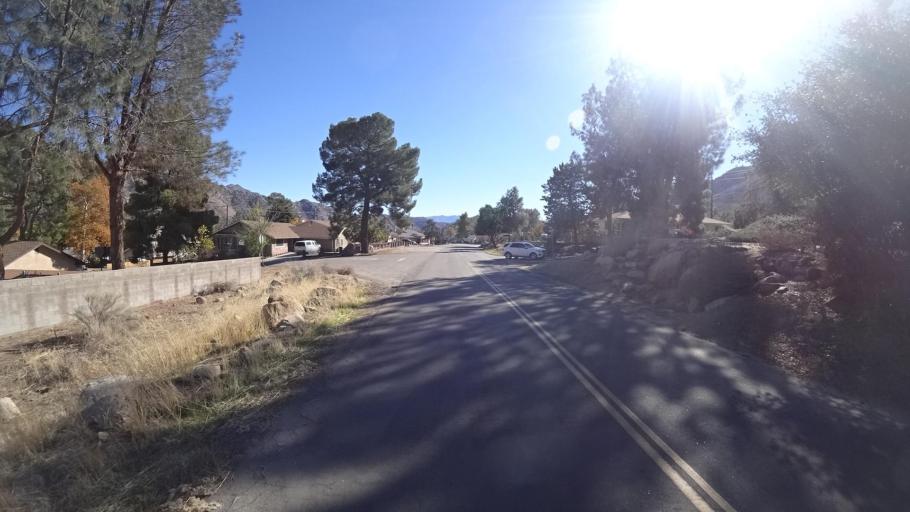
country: US
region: California
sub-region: Kern County
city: Kernville
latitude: 35.7642
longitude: -118.4317
